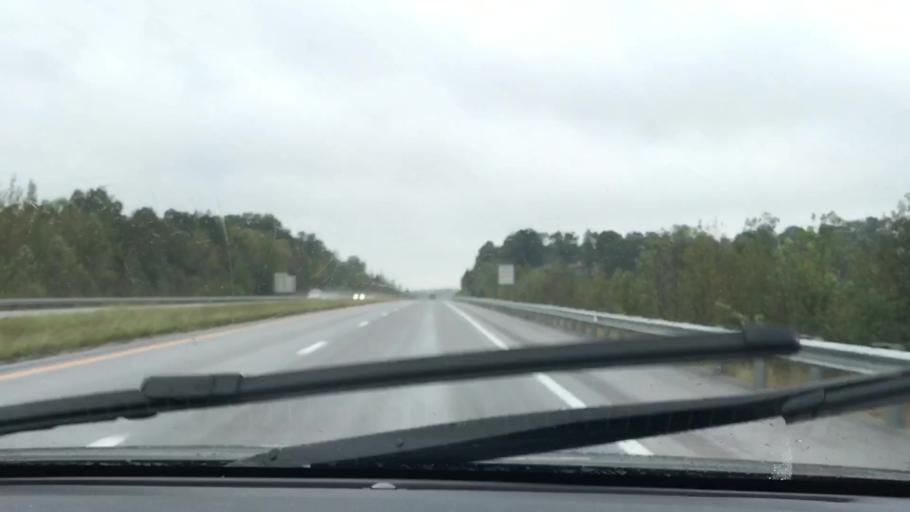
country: US
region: Kentucky
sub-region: Hopkins County
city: Nortonville
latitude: 37.1804
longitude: -87.4462
